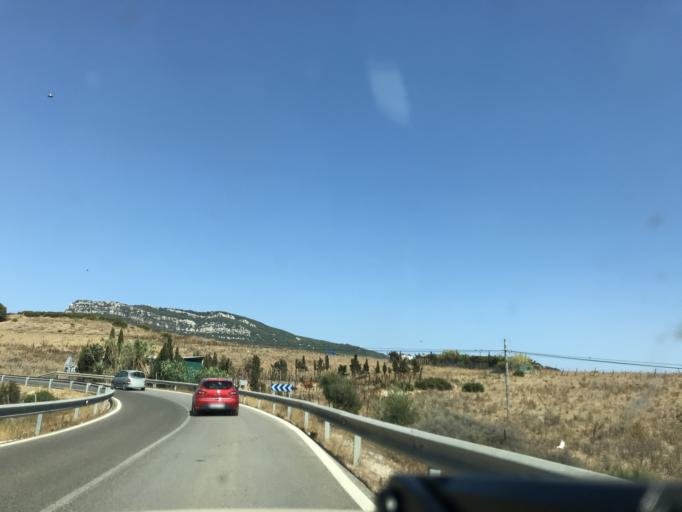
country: ES
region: Andalusia
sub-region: Provincia de Cadiz
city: Zahara de los Atunes
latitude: 36.0880
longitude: -5.7619
